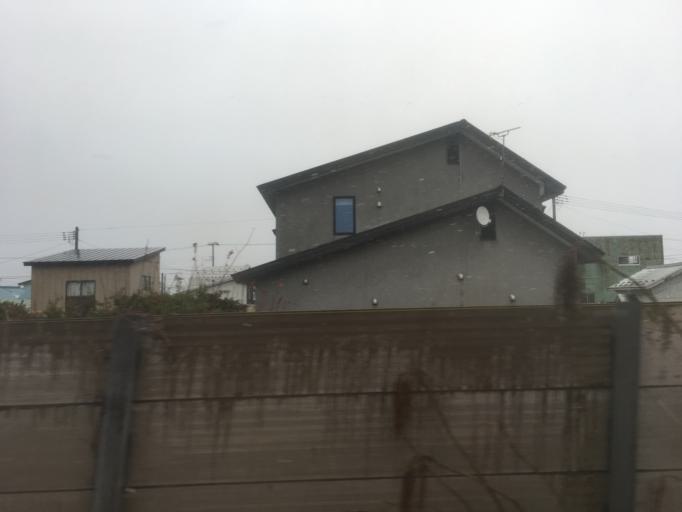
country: JP
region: Aomori
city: Aomori Shi
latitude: 40.9088
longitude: 140.6710
